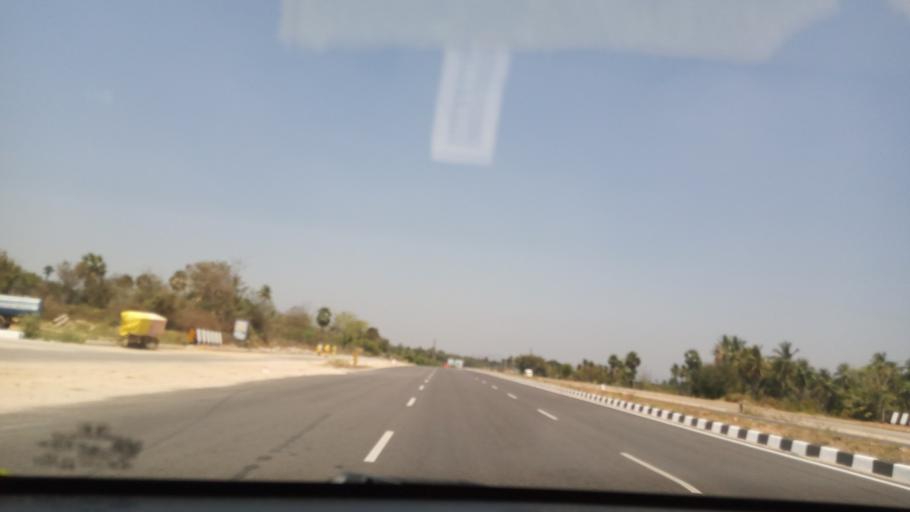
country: IN
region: Andhra Pradesh
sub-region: Chittoor
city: Pakala
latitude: 13.3962
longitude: 79.0983
